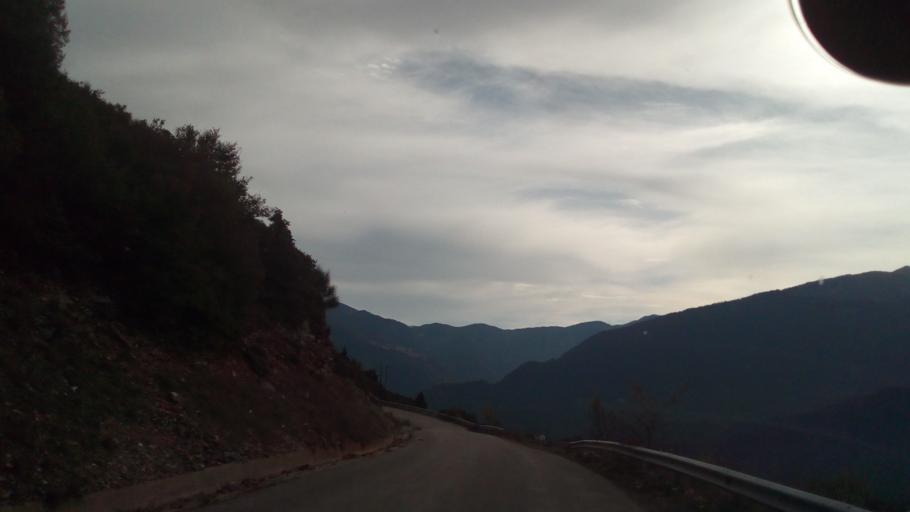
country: GR
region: West Greece
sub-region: Nomos Aitolias kai Akarnanias
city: Thermo
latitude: 38.6802
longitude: 21.8770
